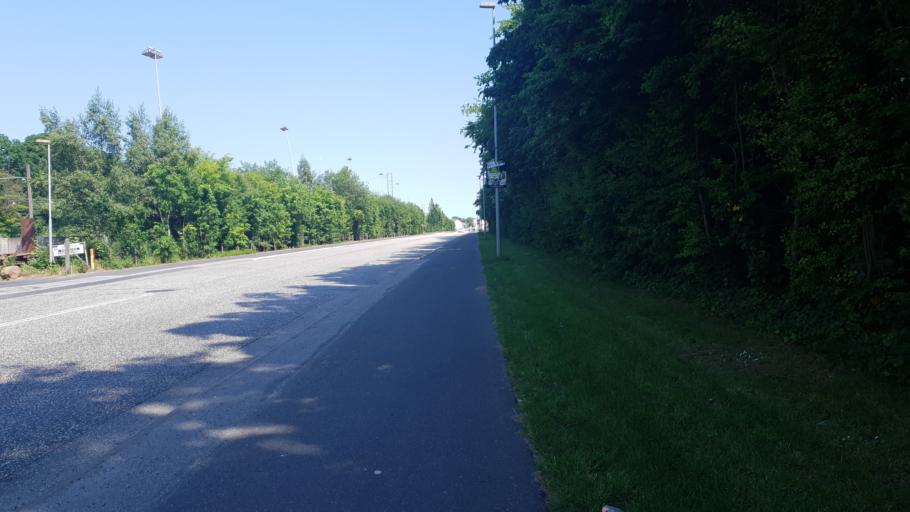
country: DK
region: South Denmark
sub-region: Fredericia Kommune
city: Fredericia
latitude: 55.5614
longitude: 9.7435
